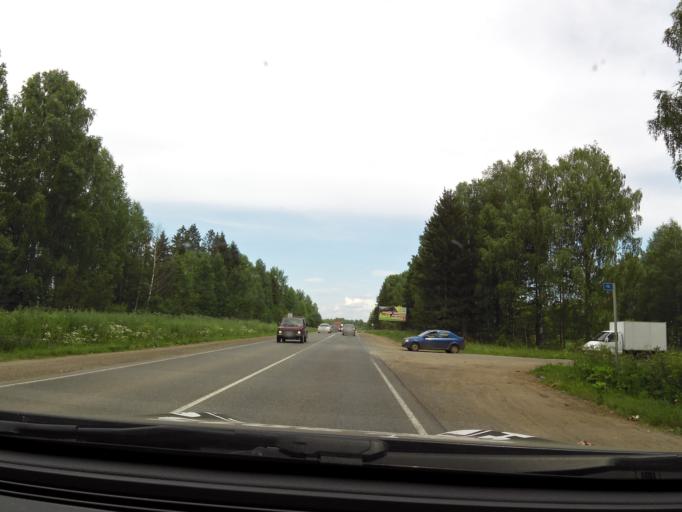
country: RU
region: Kirov
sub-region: Kirovo-Chepetskiy Rayon
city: Kirov
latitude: 58.6359
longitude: 49.8345
